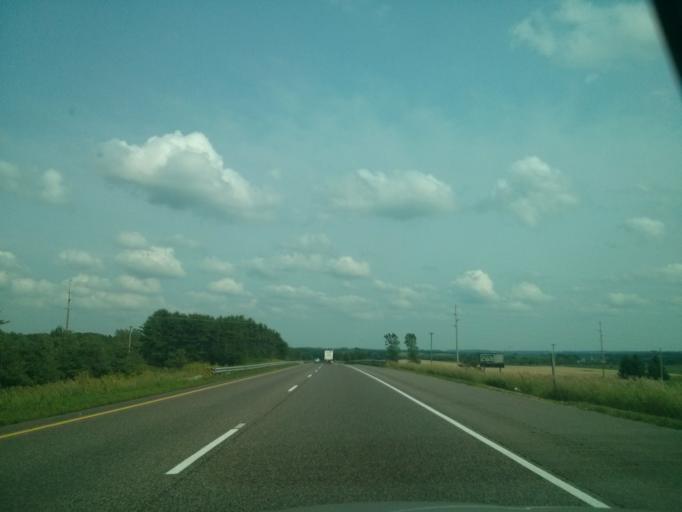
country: US
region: Wisconsin
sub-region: Saint Croix County
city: Roberts
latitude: 44.9478
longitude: -92.5394
